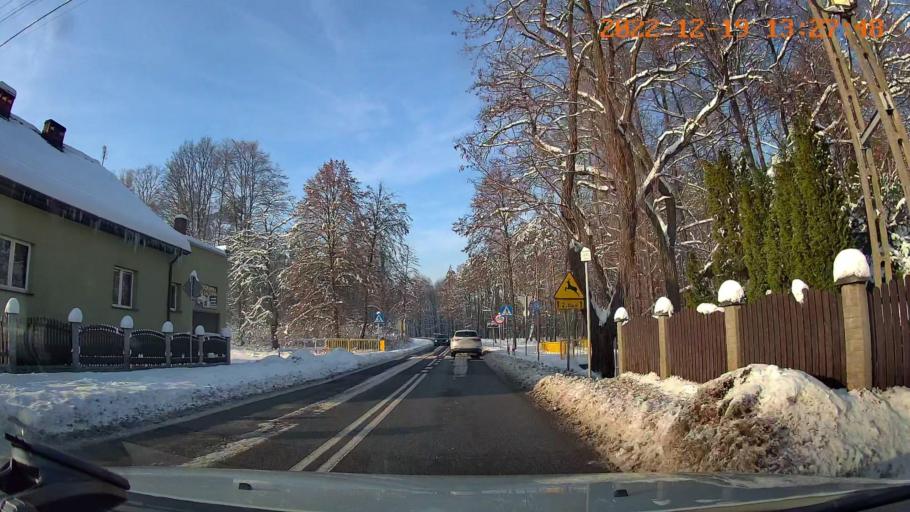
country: PL
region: Silesian Voivodeship
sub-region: Powiat bierunsko-ledzinski
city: Ledziny
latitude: 50.1089
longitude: 19.1343
